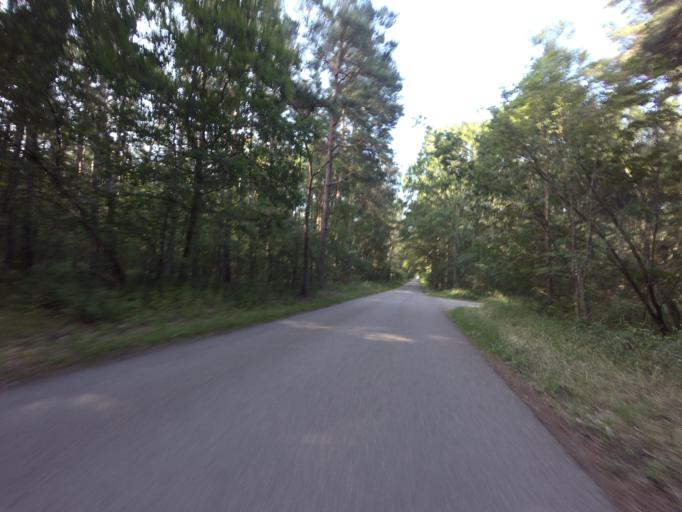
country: SE
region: Skane
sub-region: Landskrona
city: Asmundtorp
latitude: 55.8430
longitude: 12.9333
